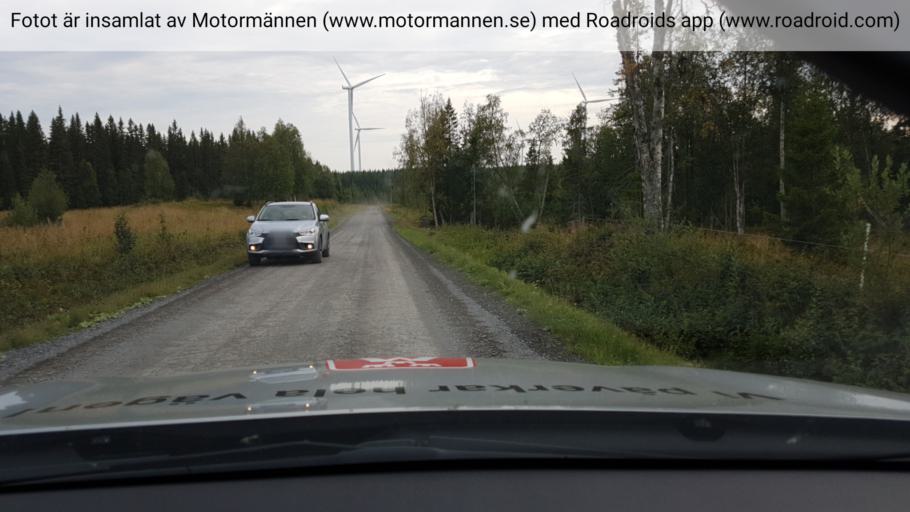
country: SE
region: Jaemtland
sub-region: OEstersunds Kommun
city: Lit
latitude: 63.6041
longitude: 14.9964
